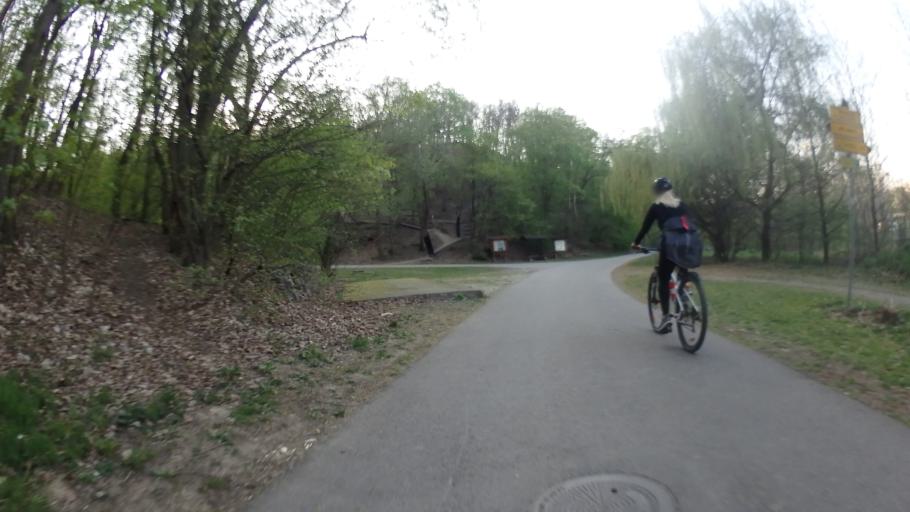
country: CZ
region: South Moravian
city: Ostopovice
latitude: 49.1853
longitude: 16.5700
